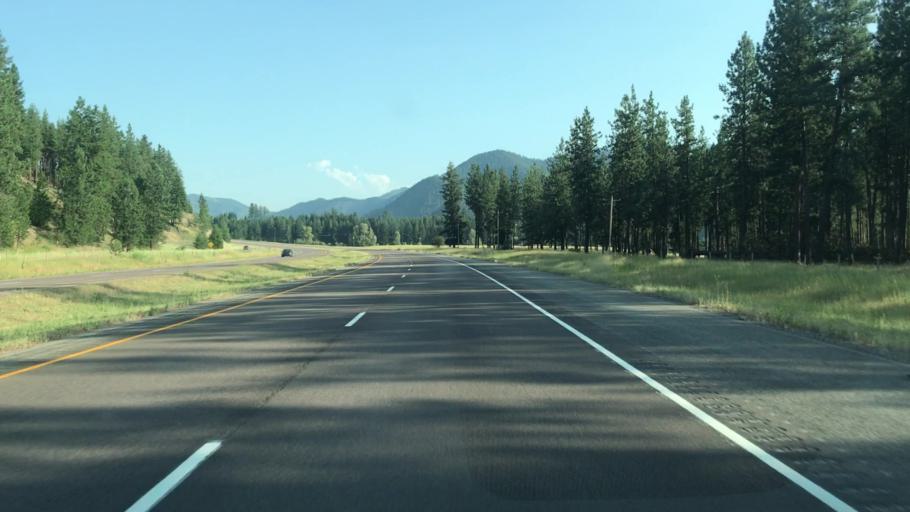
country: US
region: Montana
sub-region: Mineral County
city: Superior
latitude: 47.0612
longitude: -114.7635
